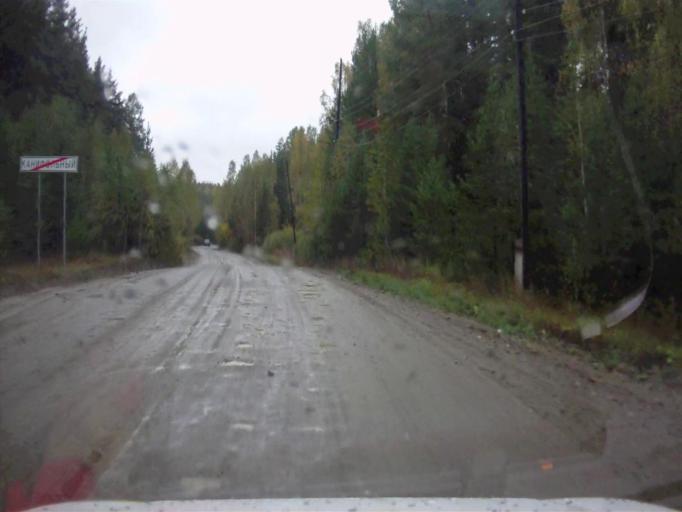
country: RU
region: Chelyabinsk
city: Kyshtym
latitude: 55.7466
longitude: 60.4913
